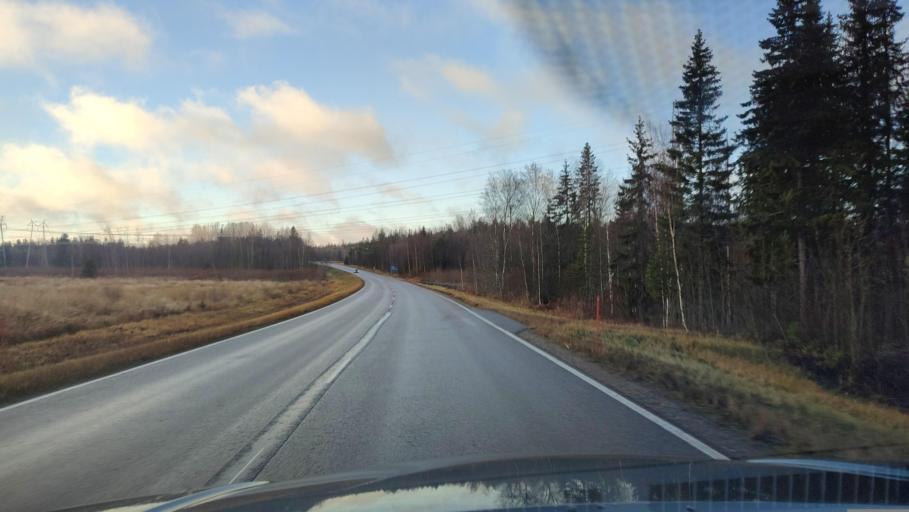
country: FI
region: Ostrobothnia
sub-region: Sydosterbotten
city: Kristinestad
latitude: 62.2981
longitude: 21.3896
